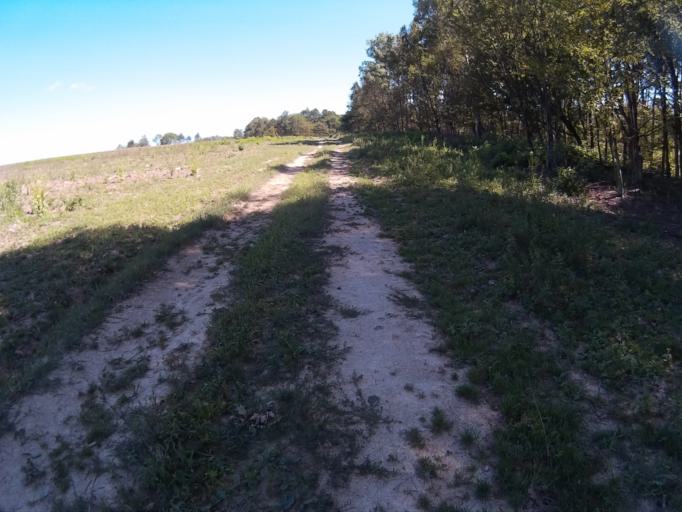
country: HU
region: Zala
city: Zalalovo
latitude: 46.8078
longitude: 16.6524
